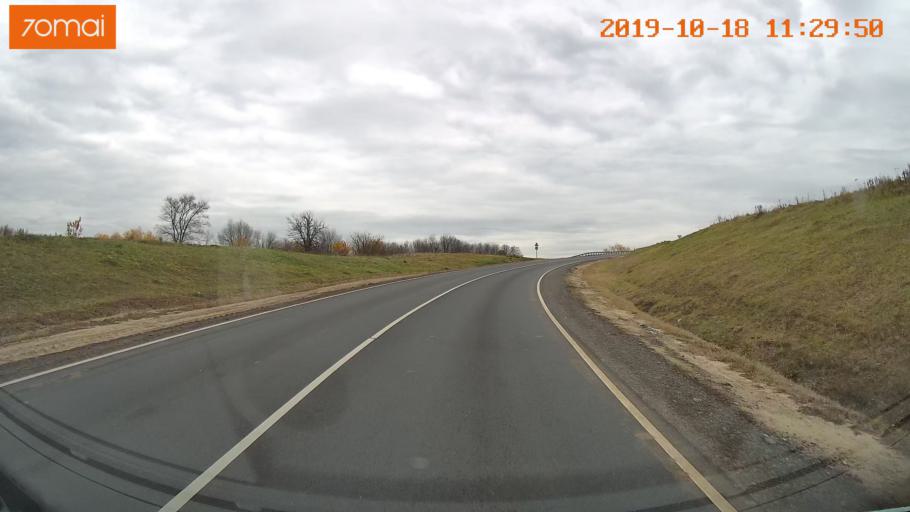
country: RU
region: Rjazan
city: Oktyabr'skiy
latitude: 54.1564
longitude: 38.6826
